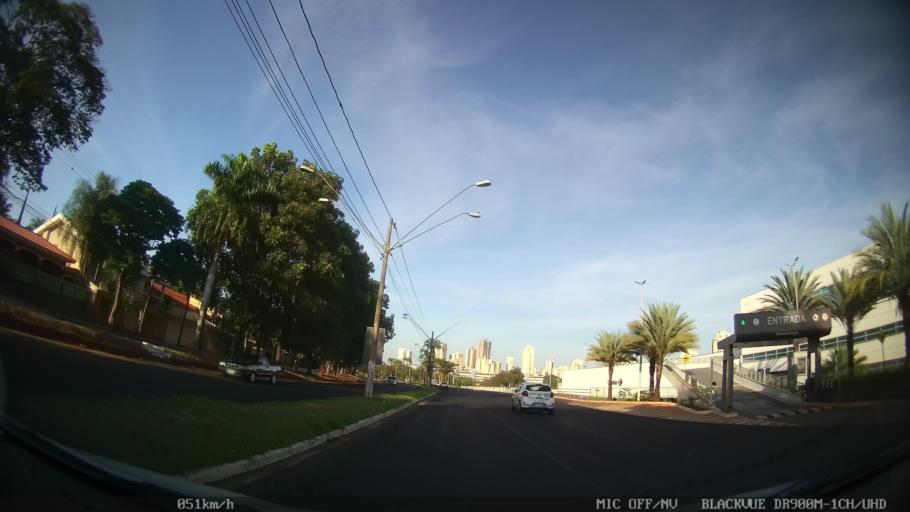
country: BR
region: Sao Paulo
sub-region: Ribeirao Preto
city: Ribeirao Preto
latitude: -21.2129
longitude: -47.8143
